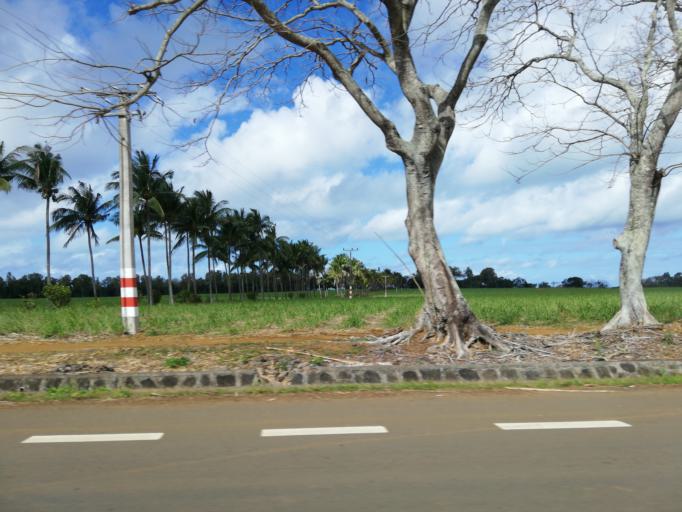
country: MU
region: Grand Port
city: Mahebourg
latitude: -20.3817
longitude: 57.6977
